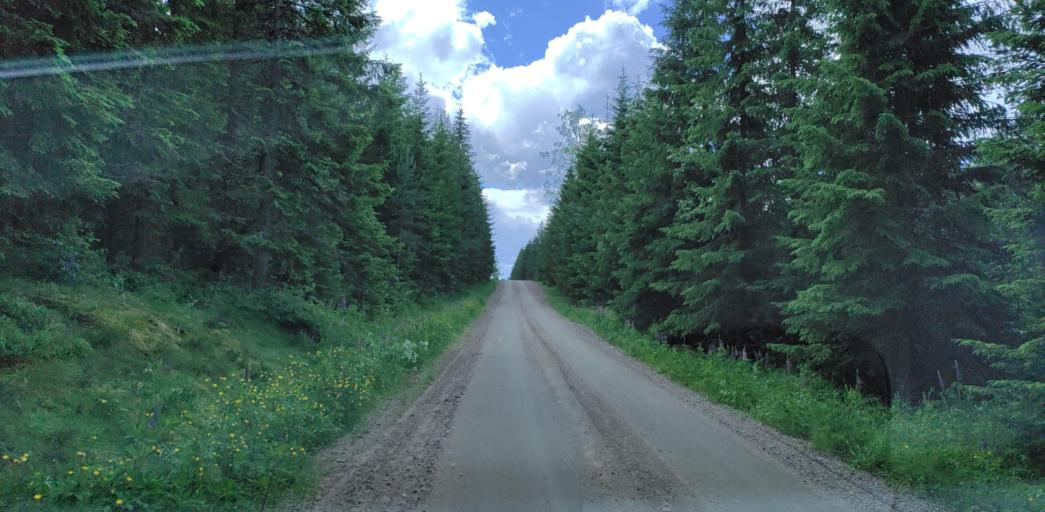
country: SE
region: Vaermland
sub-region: Hagfors Kommun
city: Ekshaerad
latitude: 60.0948
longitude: 13.3458
